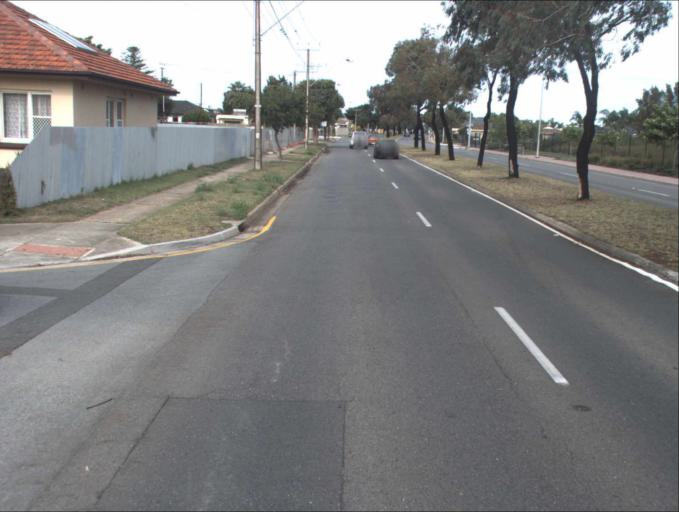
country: AU
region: South Australia
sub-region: Charles Sturt
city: Royal Park
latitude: -34.8709
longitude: 138.5034
